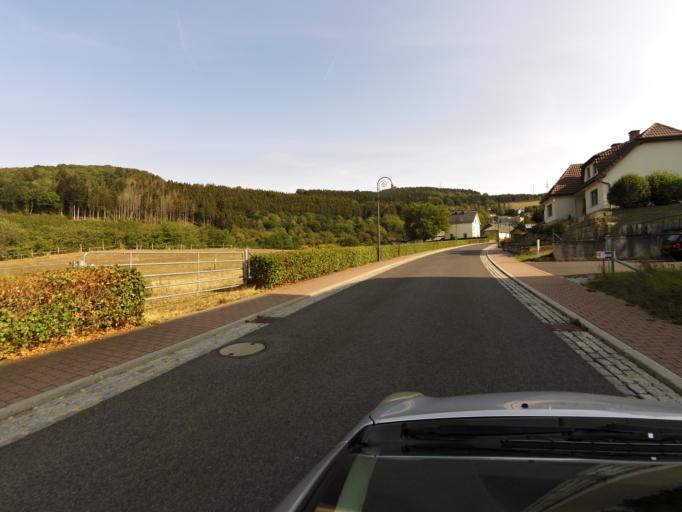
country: LU
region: Diekirch
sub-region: Canton de Diekirch
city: Bourscheid
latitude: 49.9164
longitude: 6.0831
